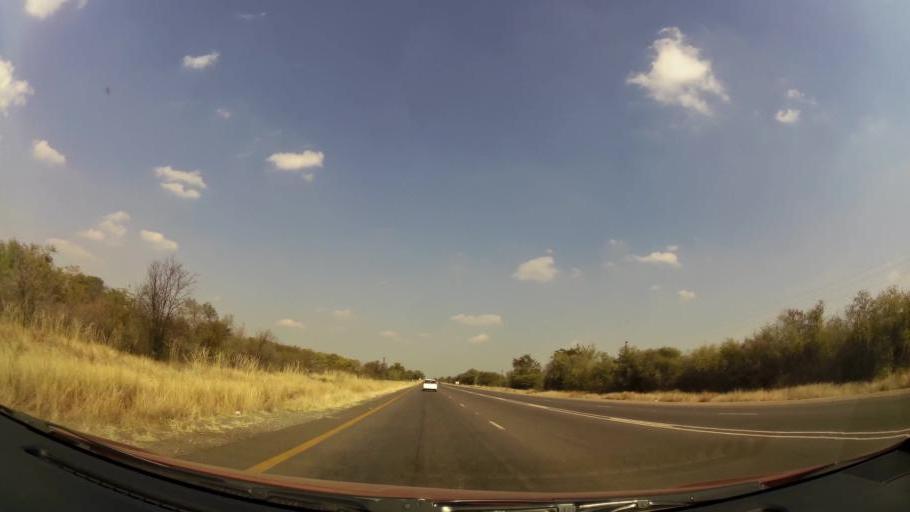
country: ZA
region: North-West
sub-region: Bojanala Platinum District Municipality
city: Mogwase
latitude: -25.4547
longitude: 27.0878
